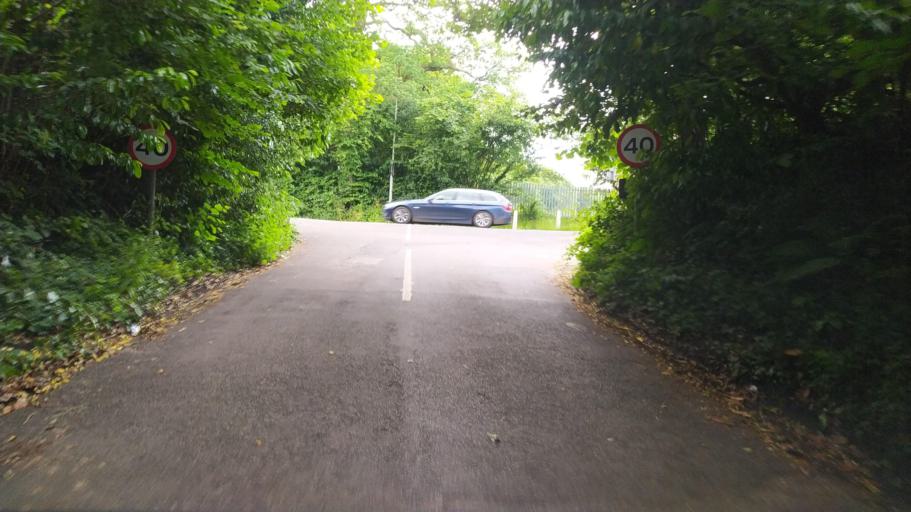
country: GB
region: England
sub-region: Hampshire
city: Liphook
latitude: 51.0856
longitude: -0.8065
